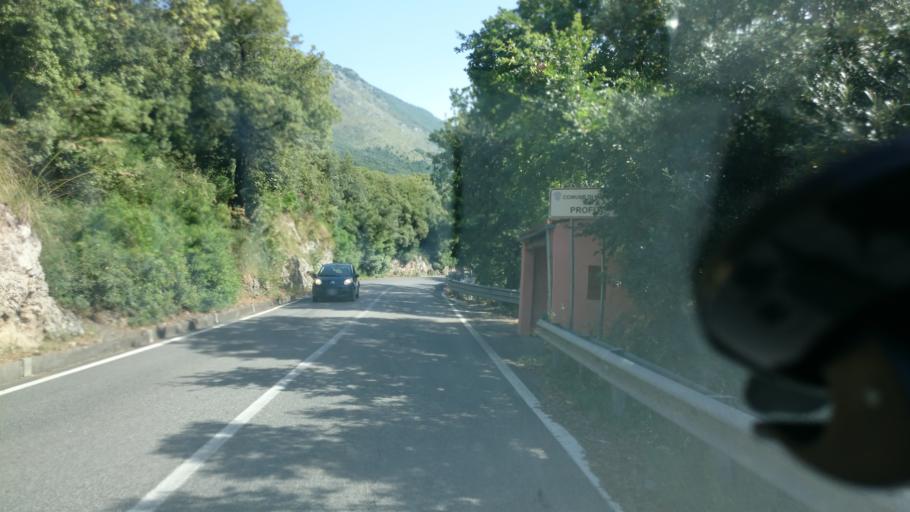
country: IT
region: Basilicate
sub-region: Provincia di Potenza
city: Maratea
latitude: 39.9930
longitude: 15.7070
